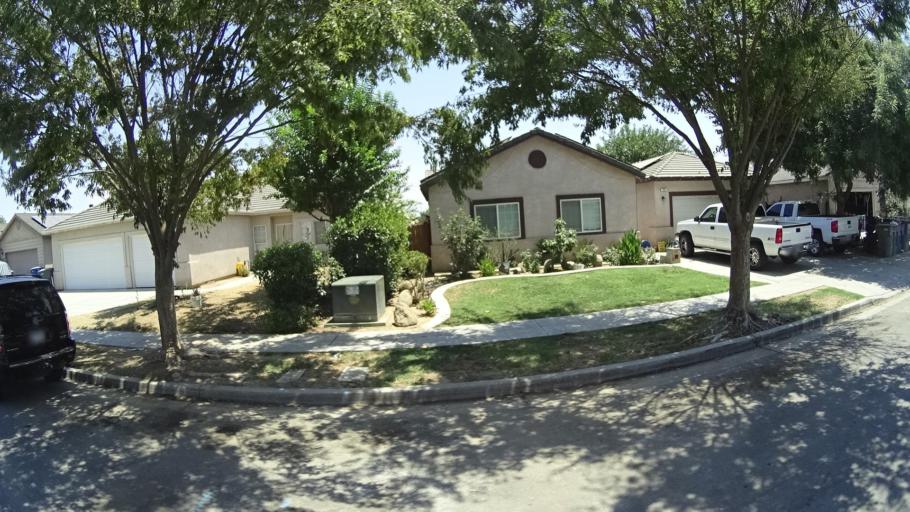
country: US
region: California
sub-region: Fresno County
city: Sunnyside
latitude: 36.7392
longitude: -119.6715
